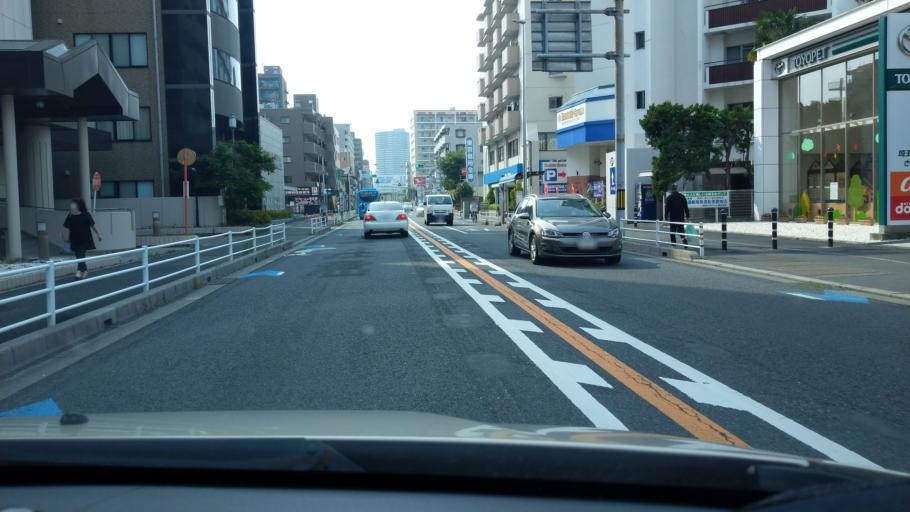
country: JP
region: Saitama
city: Shimotoda
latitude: 35.8413
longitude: 139.6575
